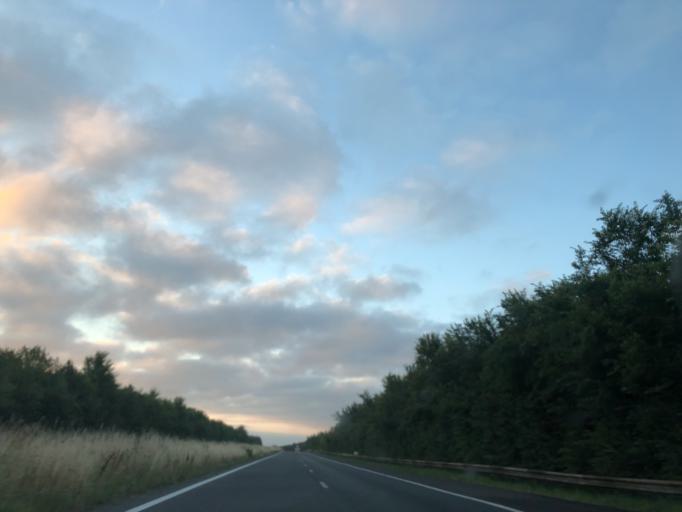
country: NL
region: Groningen
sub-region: Gemeente  Oldambt
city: Winschoten
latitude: 53.1481
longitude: 7.0740
